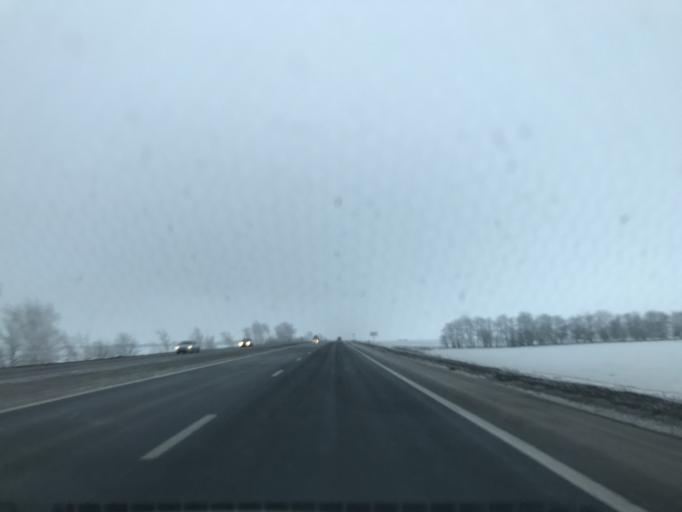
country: RU
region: Rostov
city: Grushevskaya
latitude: 47.4860
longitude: 39.9707
